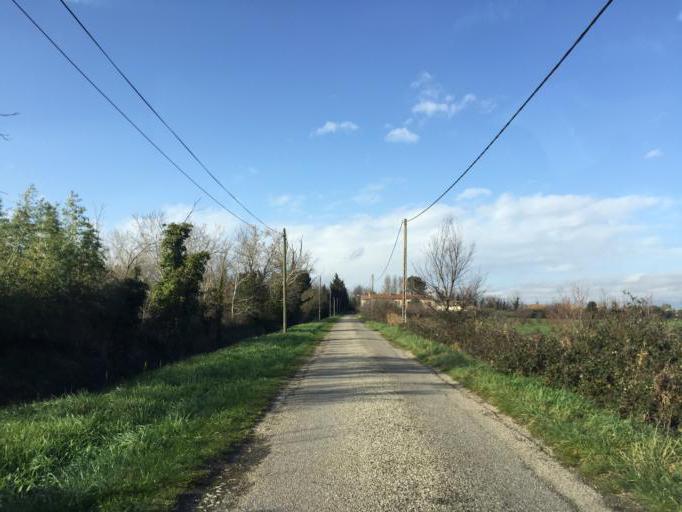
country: FR
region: Provence-Alpes-Cote d'Azur
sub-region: Departement du Vaucluse
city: Orange
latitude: 44.1381
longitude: 4.8266
